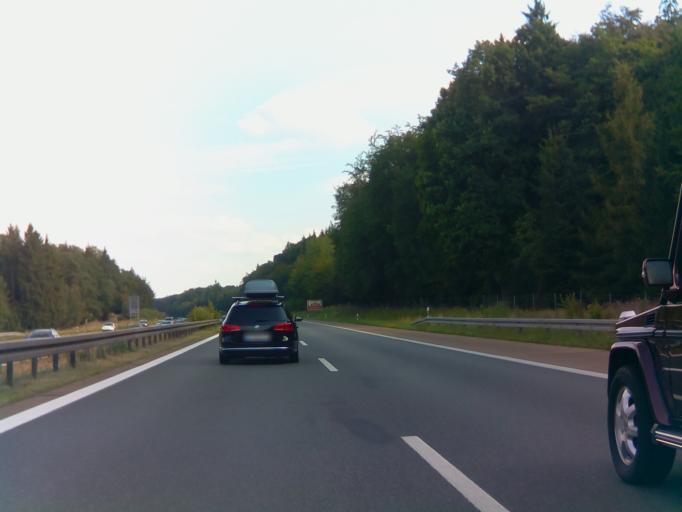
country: DE
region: Bavaria
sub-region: Regierungsbezirk Unterfranken
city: Schondra
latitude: 50.2243
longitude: 9.8981
